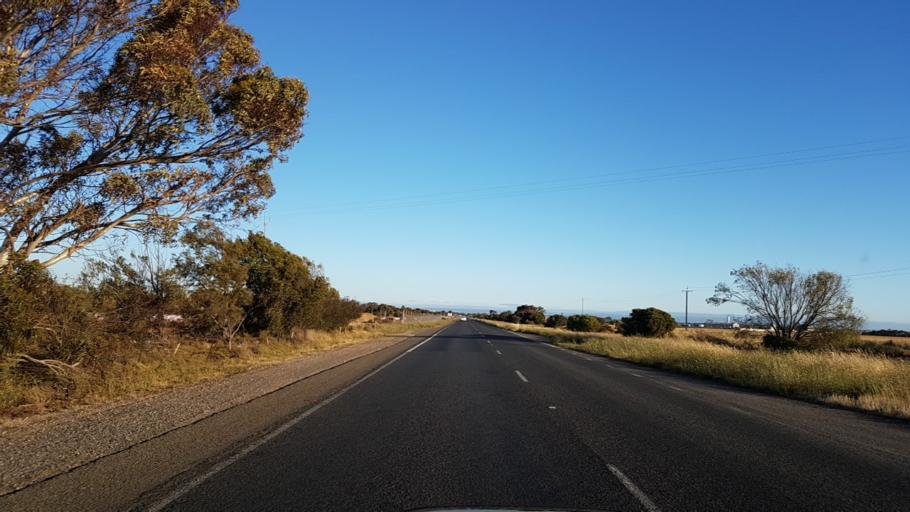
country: AU
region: South Australia
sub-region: Mallala
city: Two Wells
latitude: -34.5727
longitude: 138.4843
